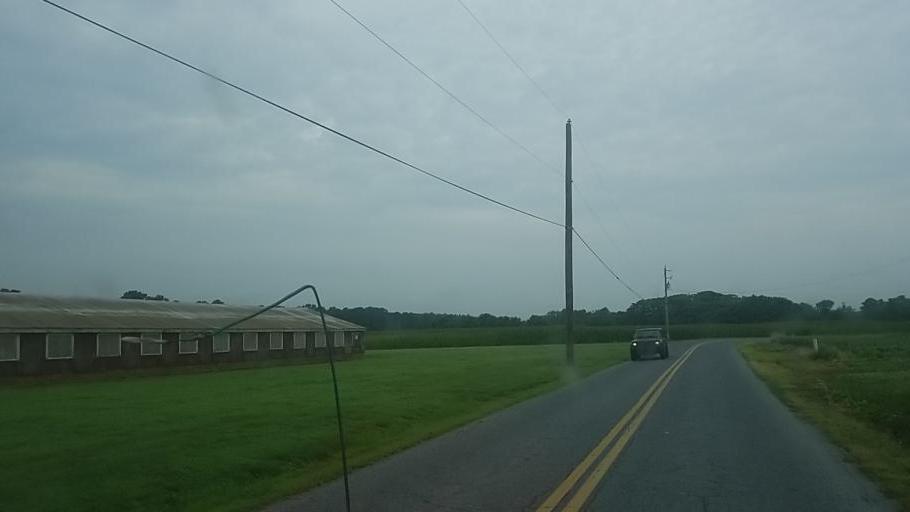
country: US
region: Delaware
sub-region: Sussex County
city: Selbyville
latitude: 38.4366
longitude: -75.1948
